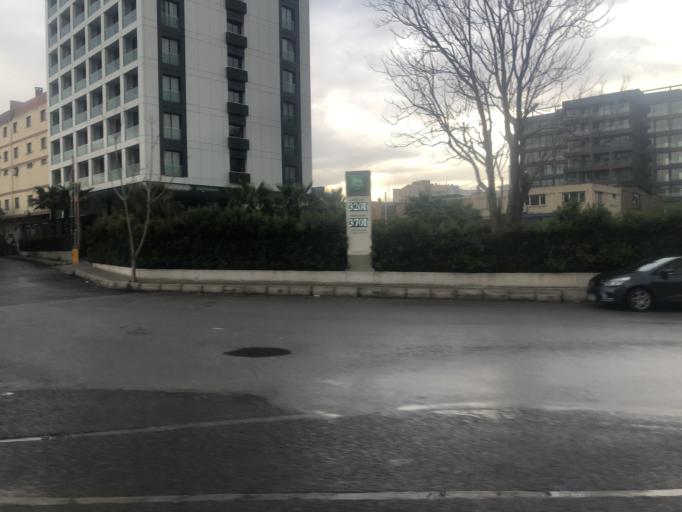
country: TR
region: Izmir
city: Bornova
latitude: 38.4509
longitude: 27.1916
